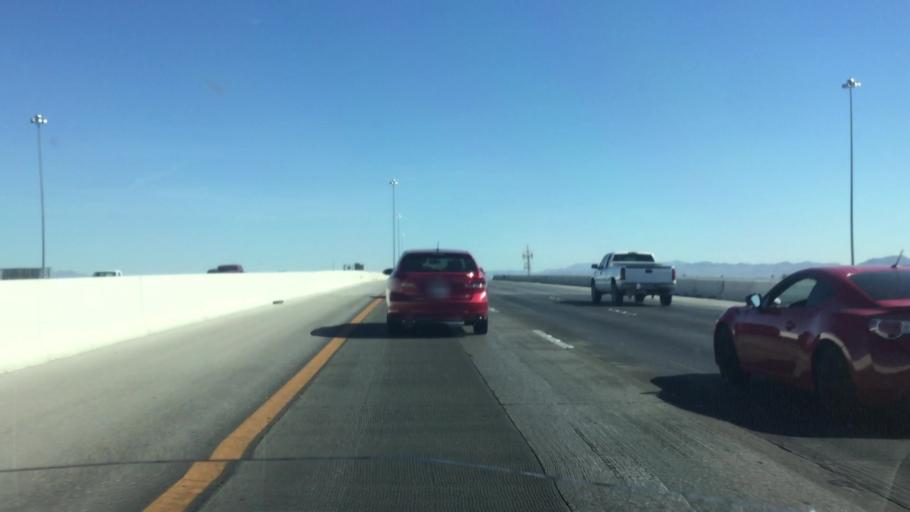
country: US
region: Nevada
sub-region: Clark County
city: Enterprise
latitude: 36.0678
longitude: -115.2086
